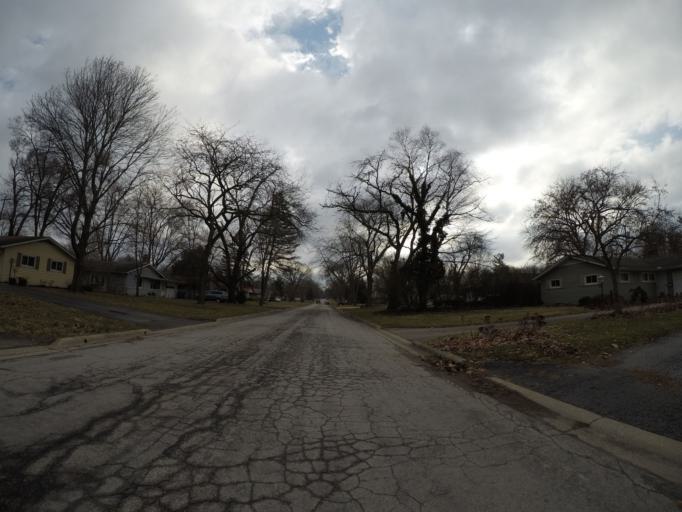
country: US
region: Ohio
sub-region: Franklin County
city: Upper Arlington
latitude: 40.0280
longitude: -83.0800
